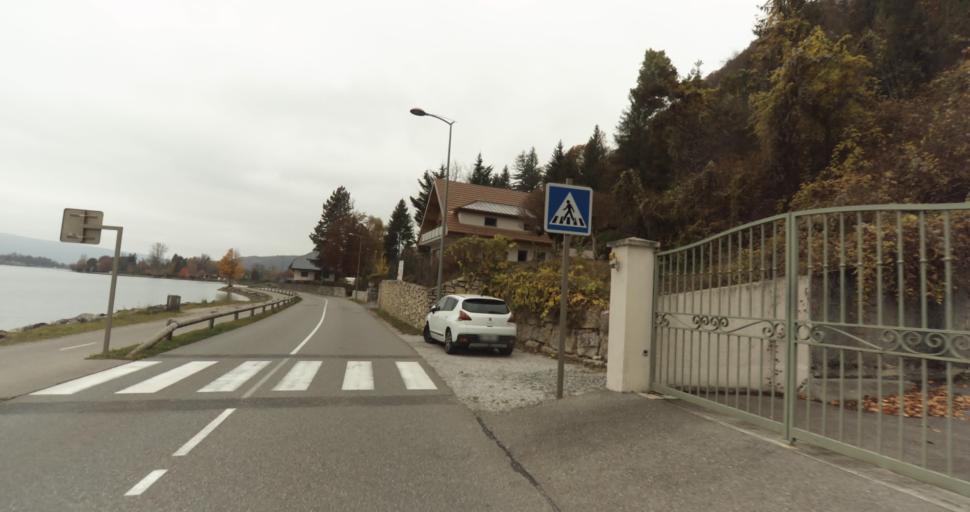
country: FR
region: Rhone-Alpes
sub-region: Departement de la Haute-Savoie
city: Talloires
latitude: 45.8199
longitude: 6.2284
